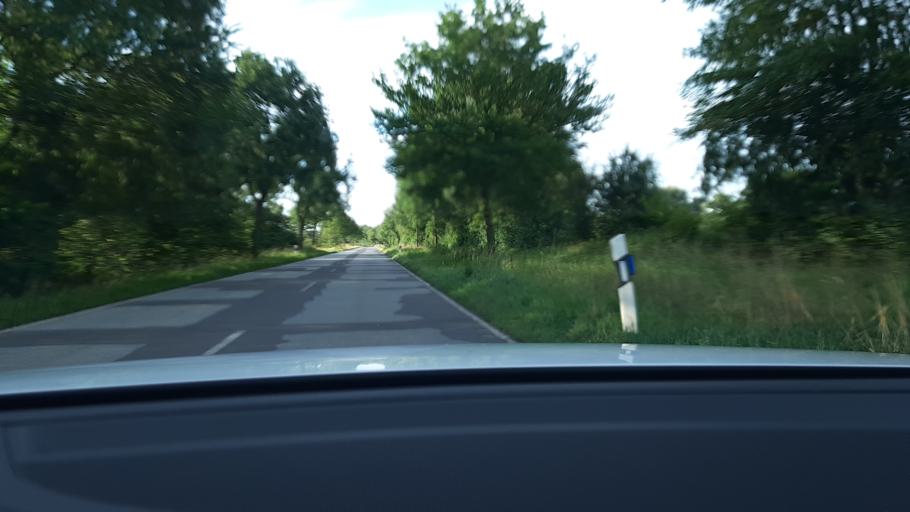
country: DE
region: Schleswig-Holstein
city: Heilshoop
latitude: 53.9007
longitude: 10.5242
